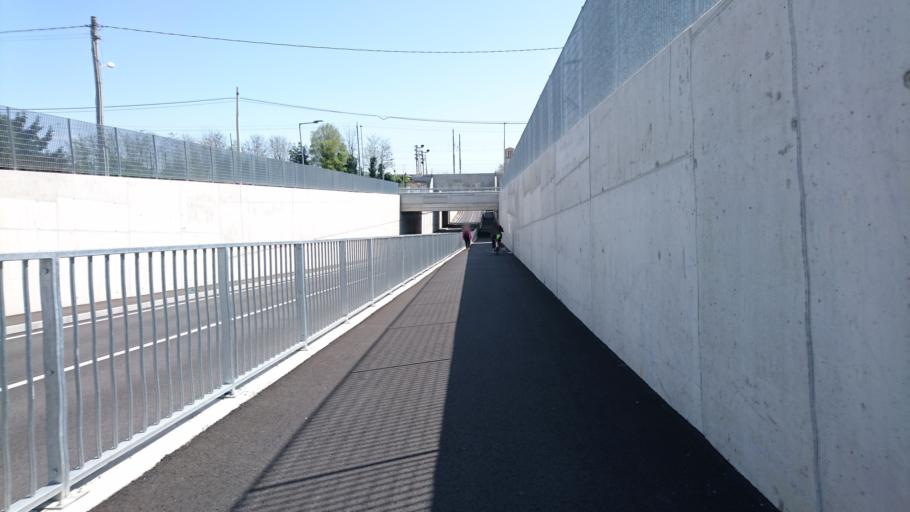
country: IT
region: Veneto
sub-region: Provincia di Padova
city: Padova
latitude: 45.4194
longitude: 11.8599
